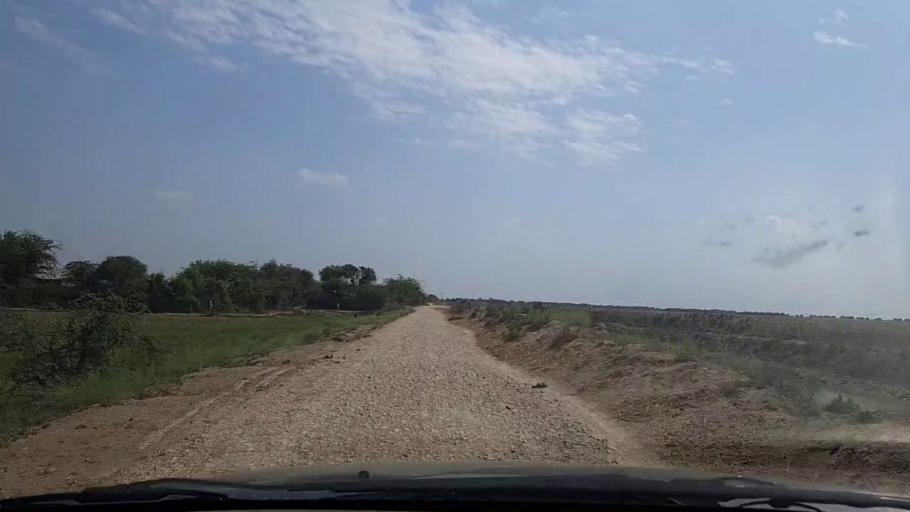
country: PK
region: Sindh
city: Mirpur Batoro
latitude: 24.5750
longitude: 68.1966
